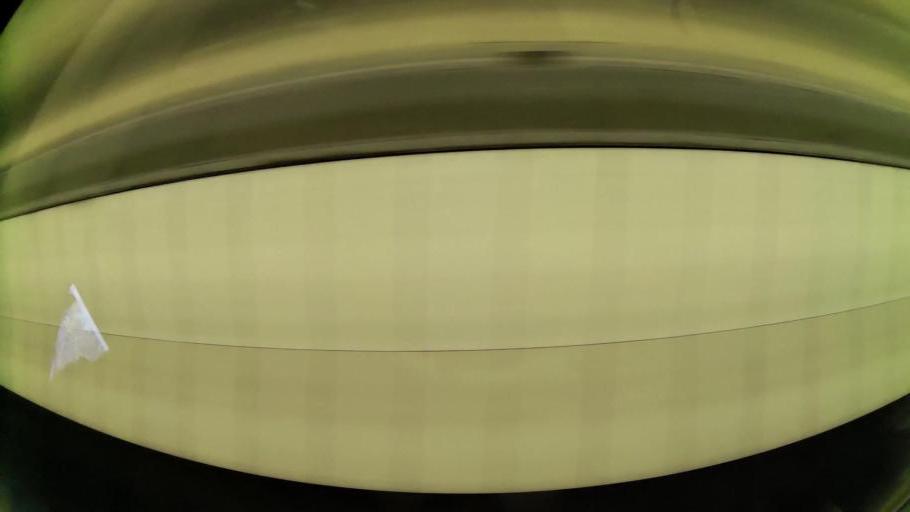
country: HK
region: Sha Tin
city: Sha Tin
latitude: 22.3782
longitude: 114.1567
